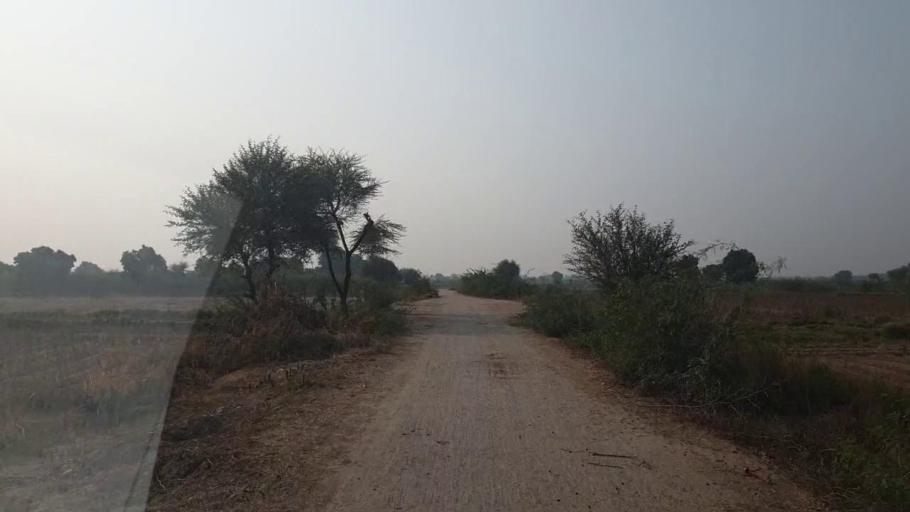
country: PK
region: Sindh
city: Tando Jam
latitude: 25.3303
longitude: 68.5262
